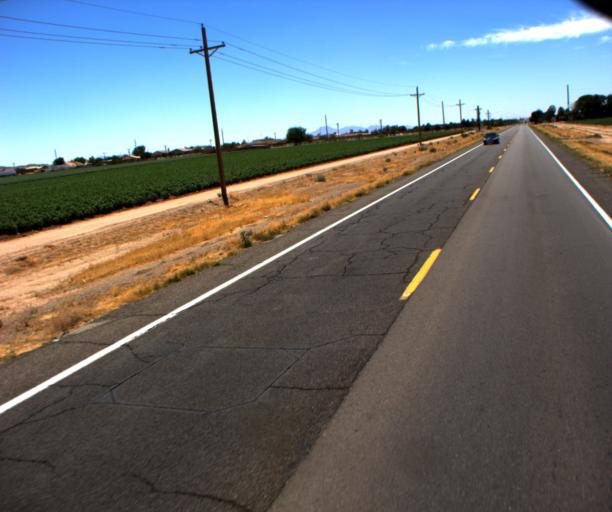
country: US
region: Arizona
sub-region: Pinal County
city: Casa Grande
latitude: 32.8797
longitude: -111.6662
